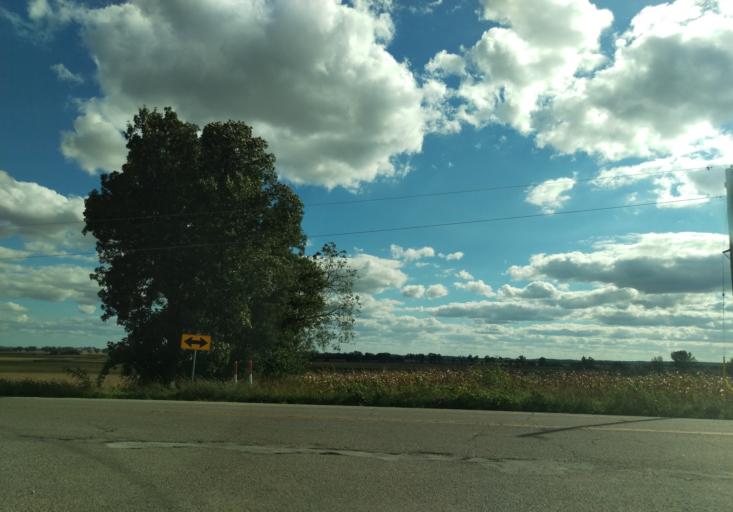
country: US
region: Wisconsin
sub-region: Rock County
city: Evansville
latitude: 42.7706
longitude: -89.2404
